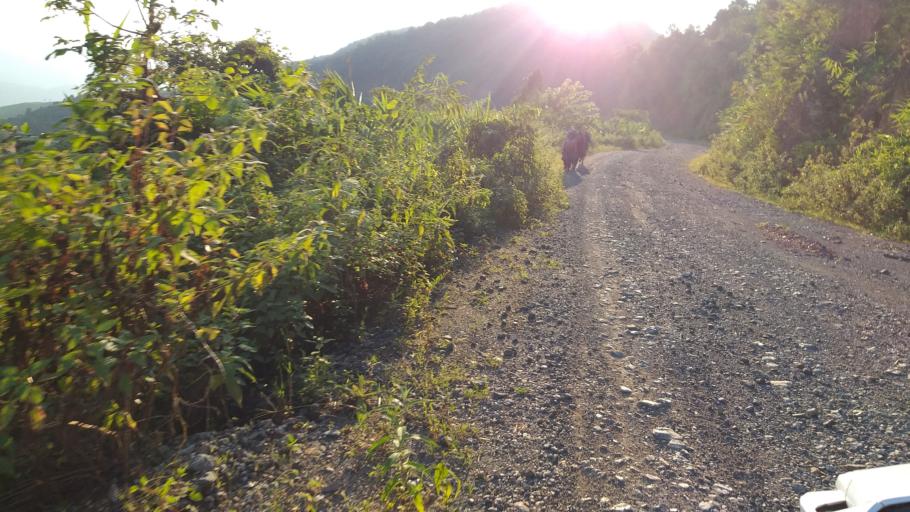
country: LA
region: Phongsali
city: Khoa
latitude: 21.1983
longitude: 102.5722
